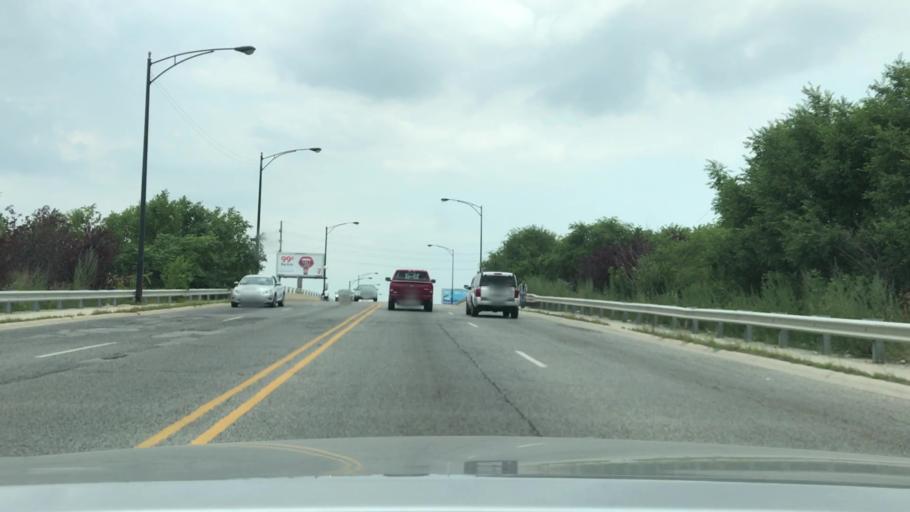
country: US
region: Illinois
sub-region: Cook County
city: Evergreen Park
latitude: 41.7564
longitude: -87.7026
